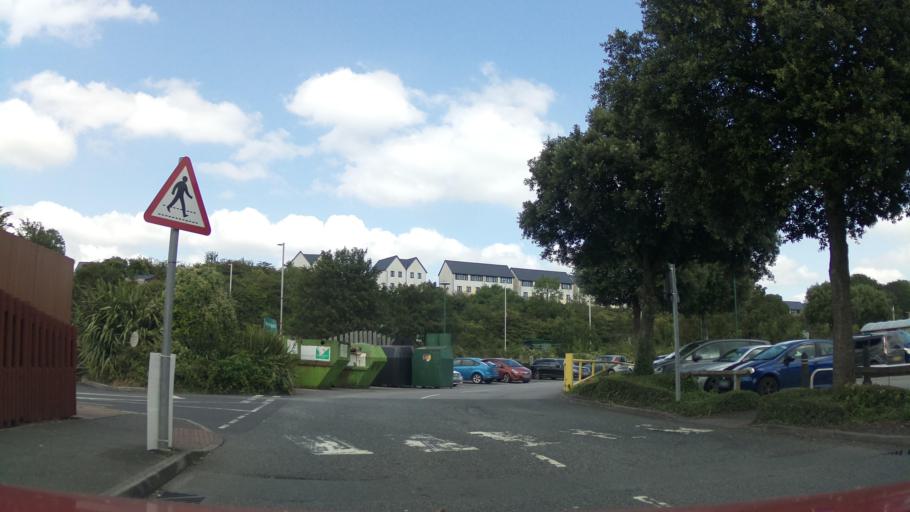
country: GB
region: England
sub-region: Plymouth
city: Plymstock
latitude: 50.3637
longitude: -4.0995
